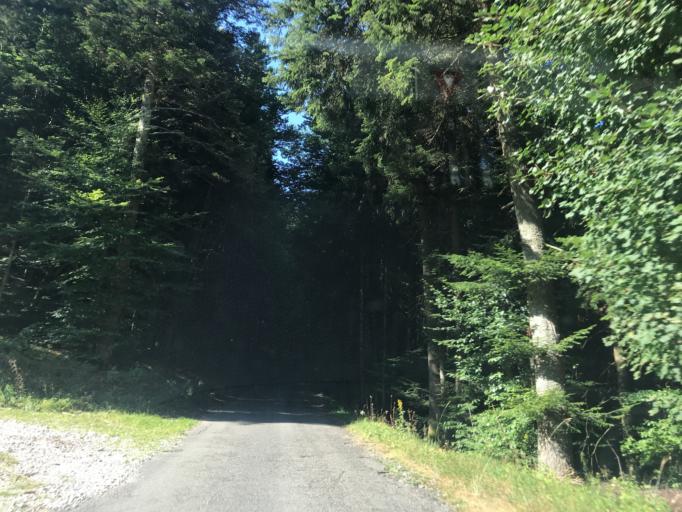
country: FR
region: Rhone-Alpes
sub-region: Departement de la Haute-Savoie
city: Thorens-Glieres
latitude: 45.9721
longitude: 6.2341
